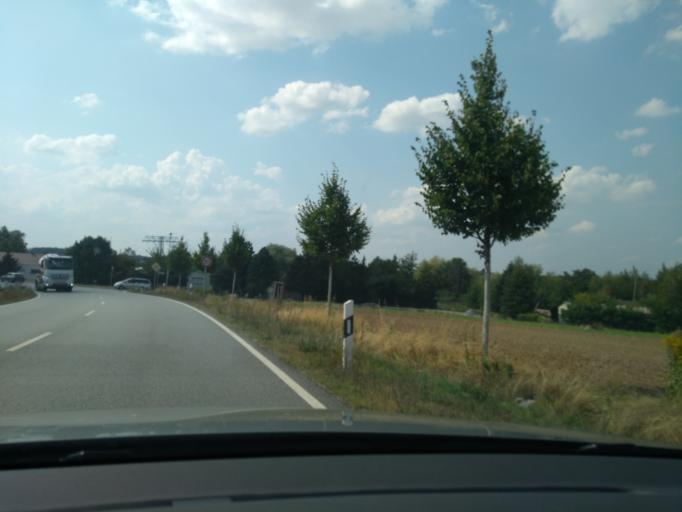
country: DE
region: Saxony
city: Bautzen
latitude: 51.1805
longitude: 14.4031
